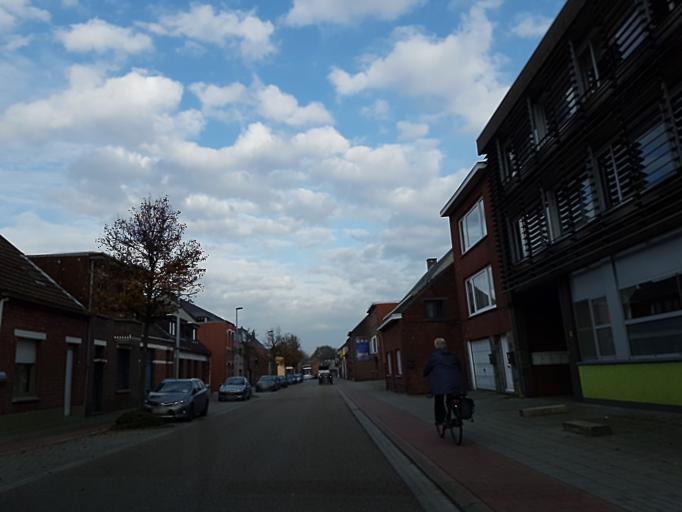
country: BE
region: Flanders
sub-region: Provincie Antwerpen
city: Kalmthout
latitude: 51.3766
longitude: 4.4736
